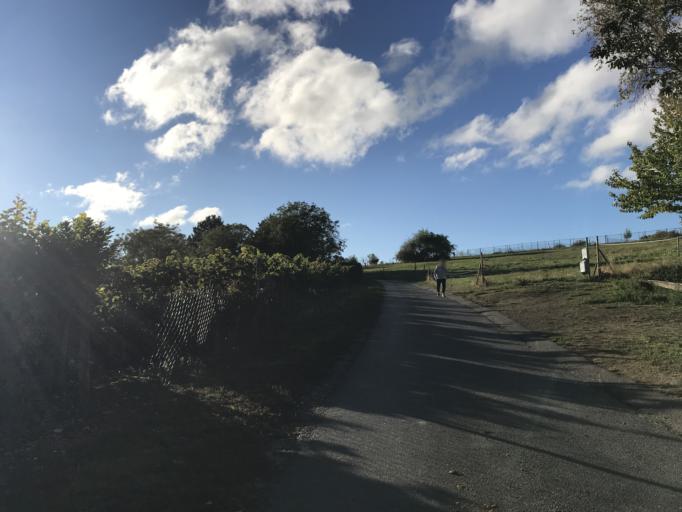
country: DE
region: Rheinland-Pfalz
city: Ober-Olm
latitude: 49.9346
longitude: 8.1869
